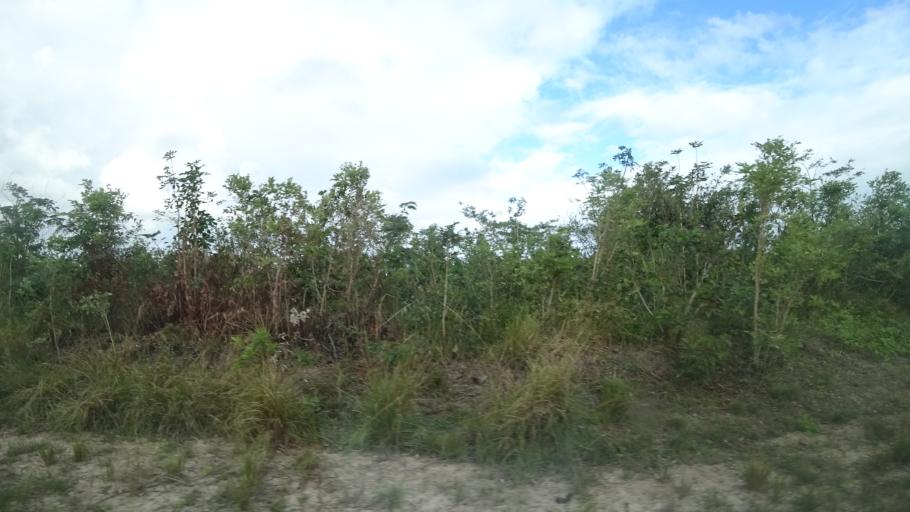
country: MZ
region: Sofala
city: Beira
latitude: -19.6650
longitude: 35.0594
